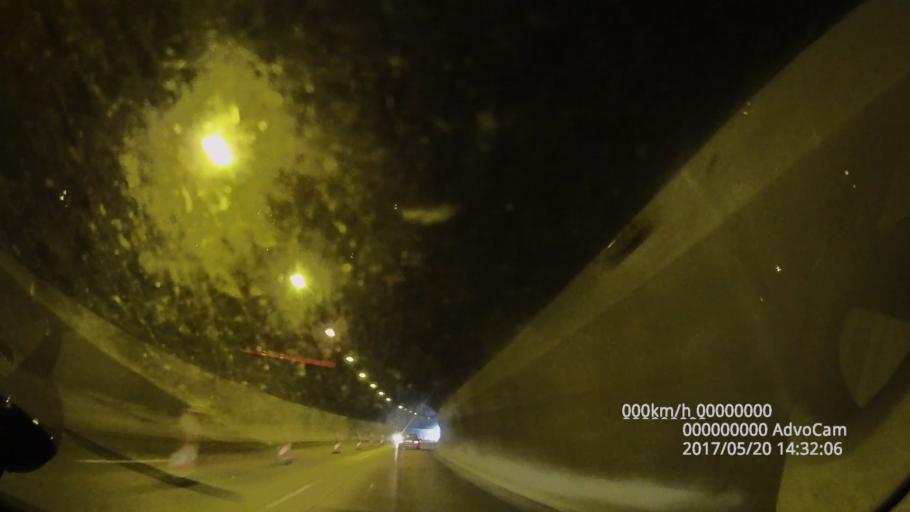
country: BG
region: Sofiya
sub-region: Obshtina Botevgrad
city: Botevgrad
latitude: 42.7792
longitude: 23.7950
